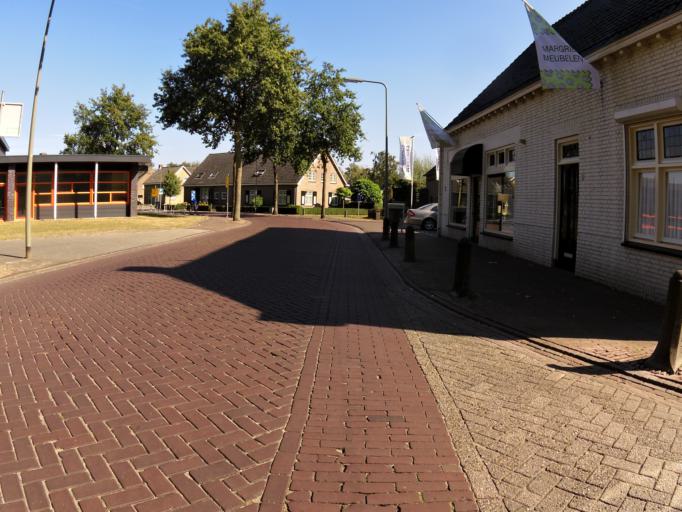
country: NL
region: North Brabant
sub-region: Gemeente Maasdonk
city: Geffen
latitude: 51.7427
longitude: 5.4636
